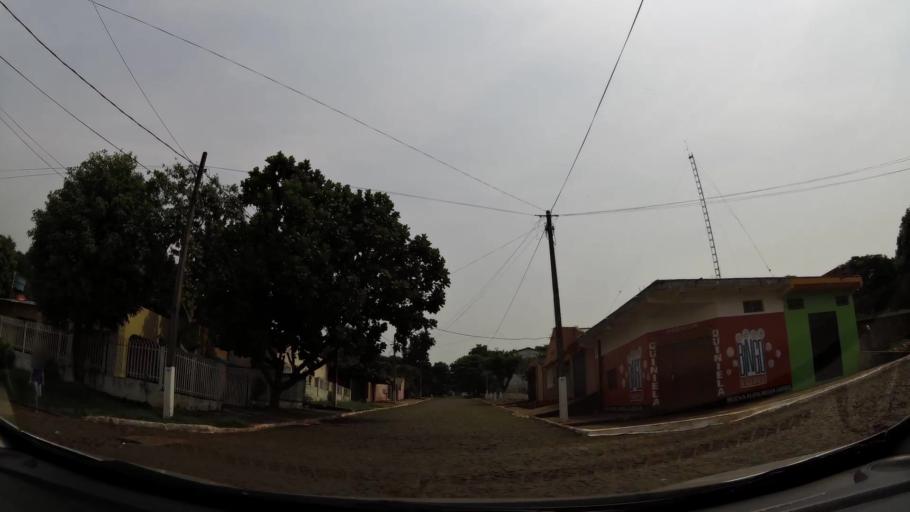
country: BR
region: Parana
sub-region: Foz Do Iguacu
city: Foz do Iguacu
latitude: -25.5663
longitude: -54.6059
